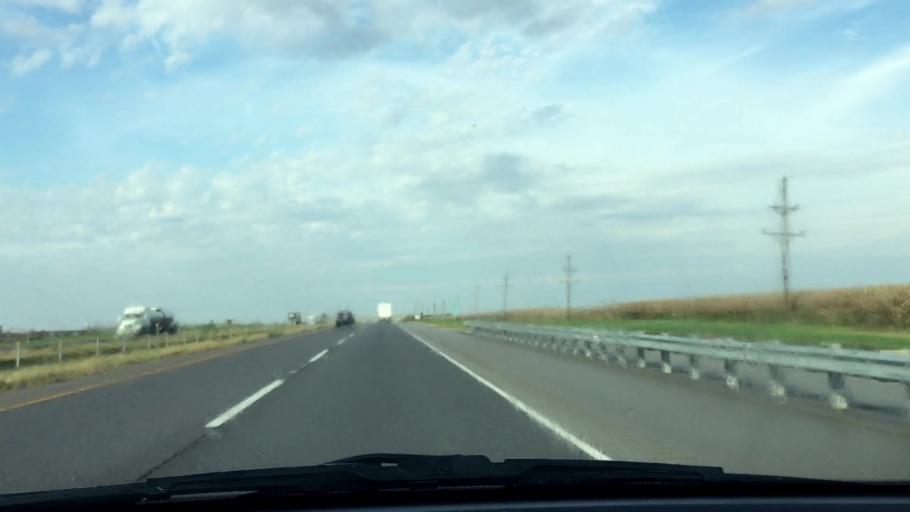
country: US
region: Illinois
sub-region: Lee County
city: Franklin Grove
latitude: 41.8229
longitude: -89.3522
